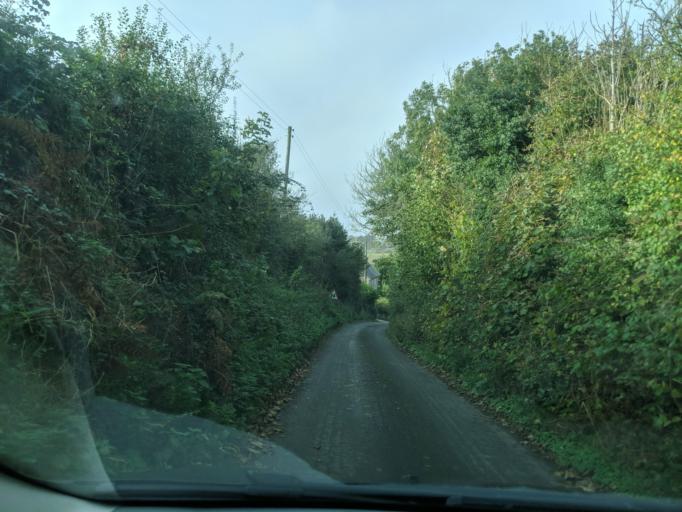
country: GB
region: England
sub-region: Cornwall
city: Looe
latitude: 50.3678
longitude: -4.4153
